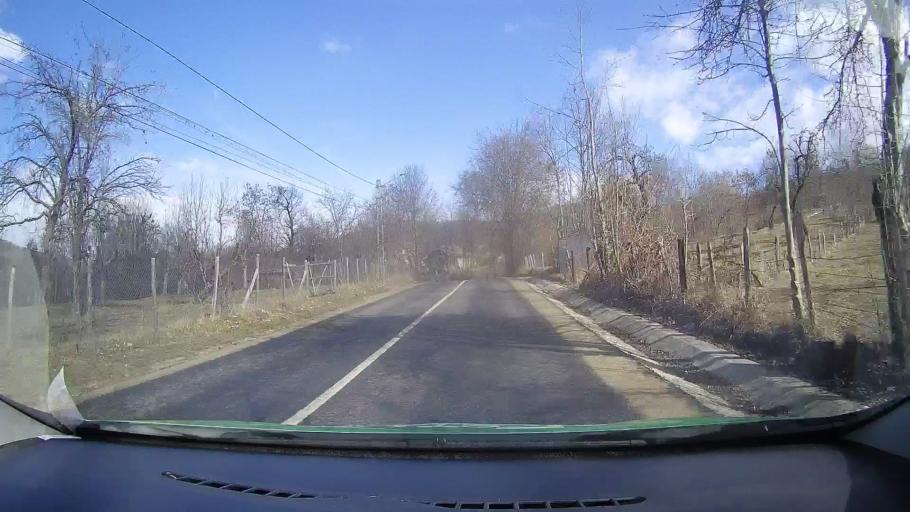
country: RO
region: Dambovita
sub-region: Comuna Runcu
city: Badeni
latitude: 45.1430
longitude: 25.4041
